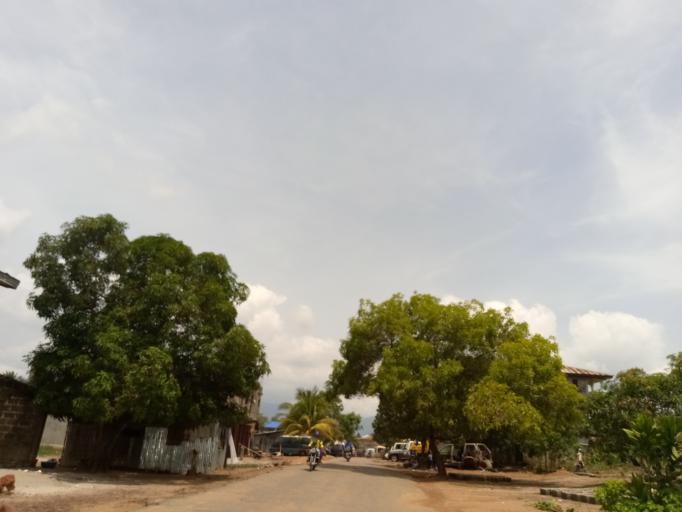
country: SL
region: Western Area
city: Waterloo
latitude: 8.3341
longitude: -13.0389
